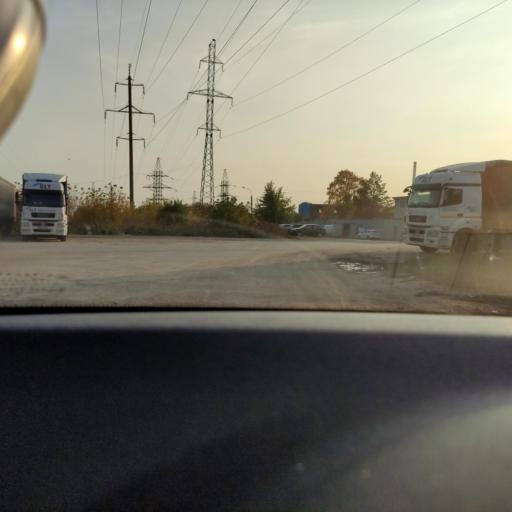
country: RU
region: Samara
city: Petra-Dubrava
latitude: 53.2628
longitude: 50.2994
